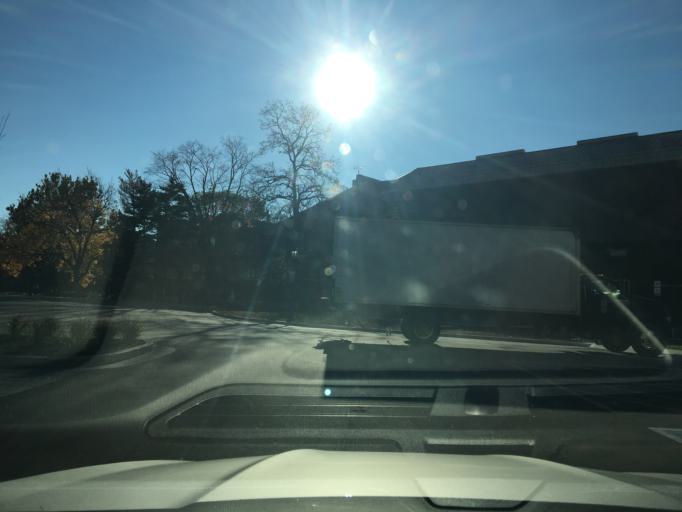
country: US
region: Indiana
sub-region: Tippecanoe County
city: West Lafayette
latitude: 40.4282
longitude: -86.9154
